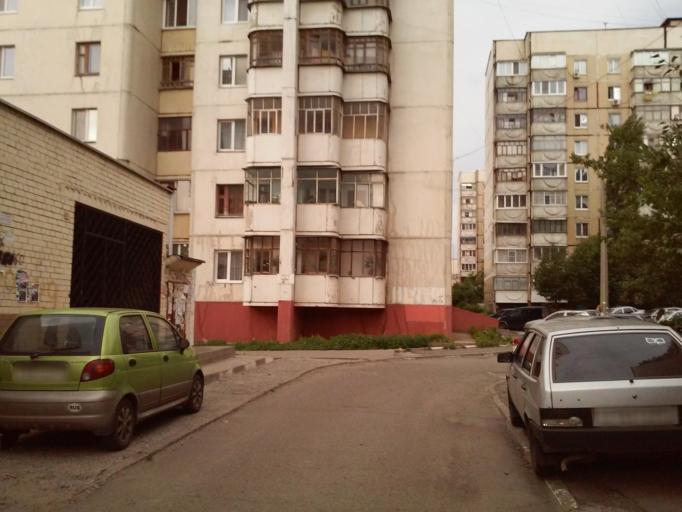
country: RU
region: Belgorod
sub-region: Belgorodskiy Rayon
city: Belgorod
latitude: 50.5673
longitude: 36.5755
